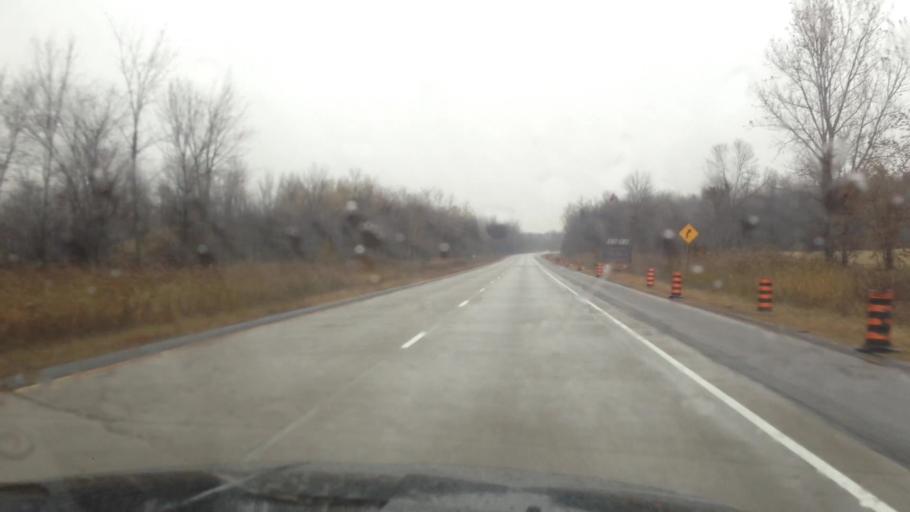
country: CA
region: Ontario
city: Hawkesbury
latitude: 45.4395
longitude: -74.7358
